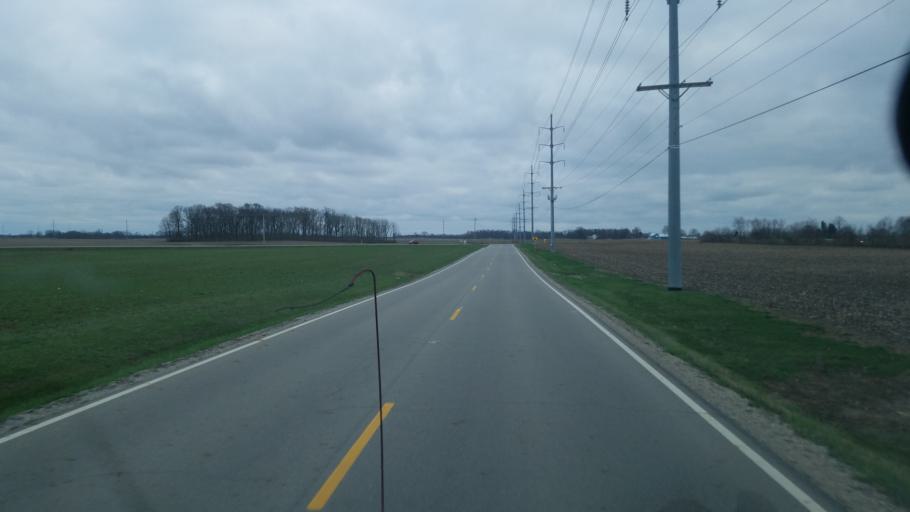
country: US
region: Ohio
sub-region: Fayette County
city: Washington Court House
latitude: 39.5203
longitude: -83.4711
